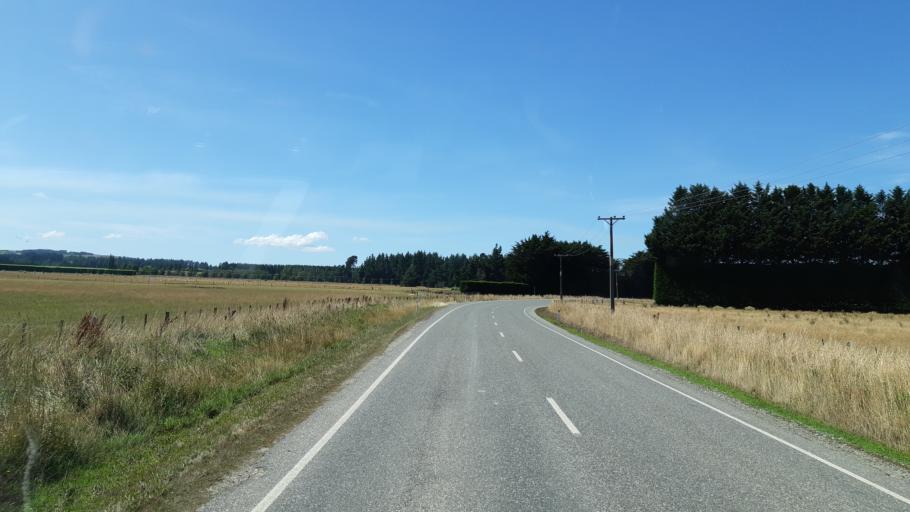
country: NZ
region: Southland
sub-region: Gore District
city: Gore
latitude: -46.0011
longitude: 168.8657
